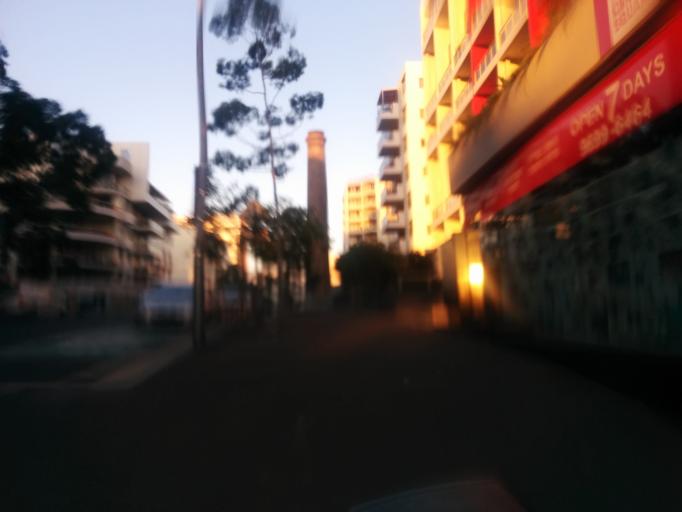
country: AU
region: New South Wales
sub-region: City of Sydney
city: Redfern
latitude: -33.8994
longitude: 151.2122
